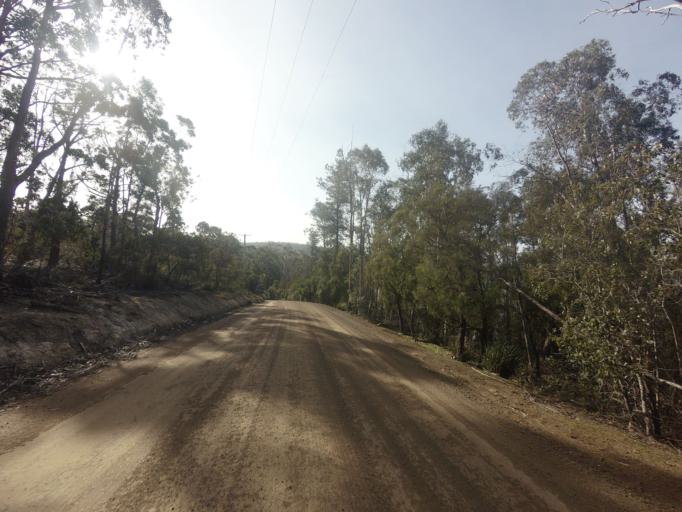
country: AU
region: Tasmania
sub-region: Kingborough
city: Kettering
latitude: -43.1173
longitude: 147.2705
